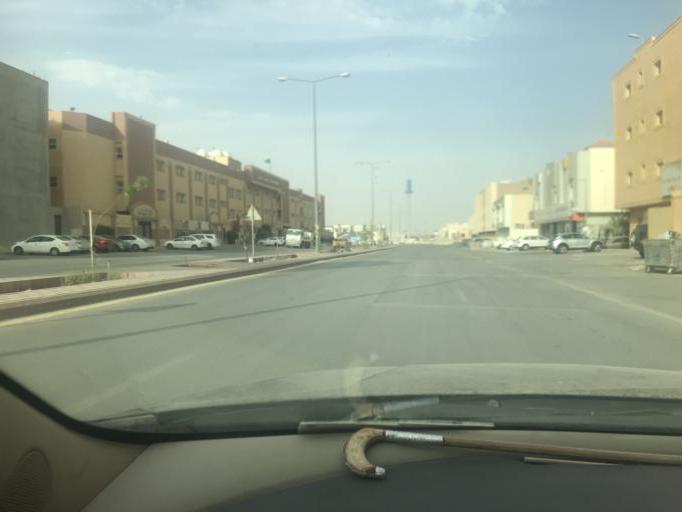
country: SA
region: Ar Riyad
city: Riyadh
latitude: 24.8017
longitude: 46.6709
